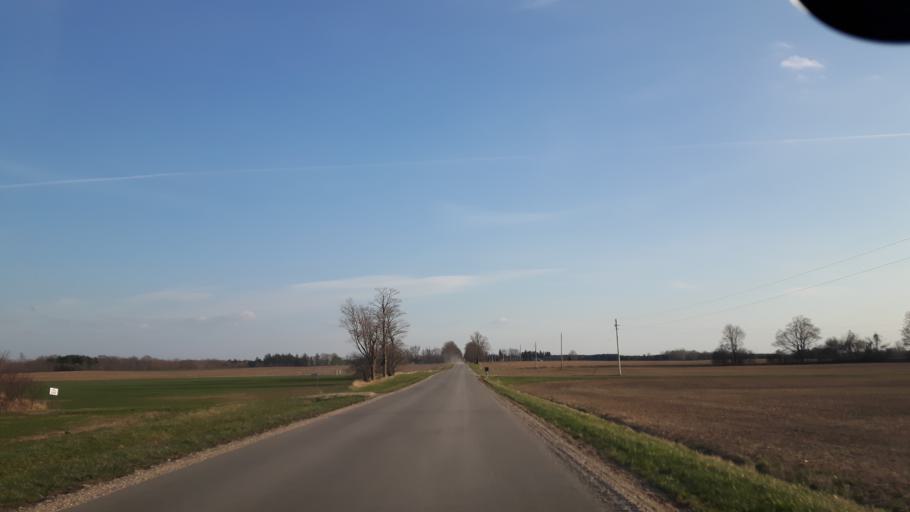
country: CA
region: Ontario
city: Goderich
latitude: 43.6340
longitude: -81.6643
